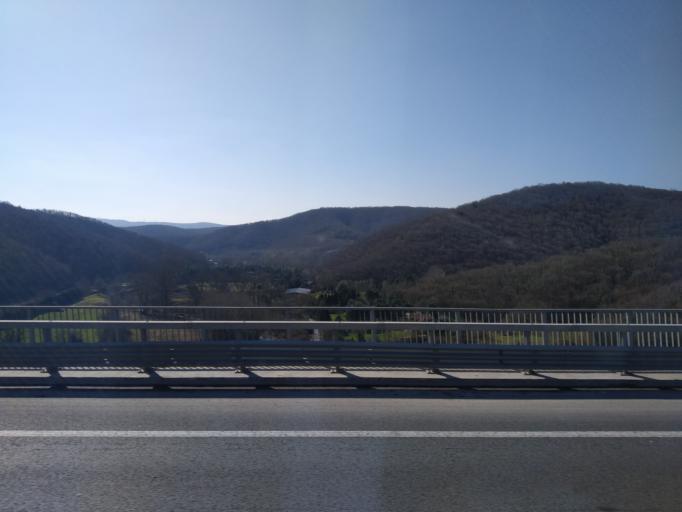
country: TR
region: Istanbul
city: Mahmut Sevket Pasa
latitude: 41.1540
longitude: 29.2674
